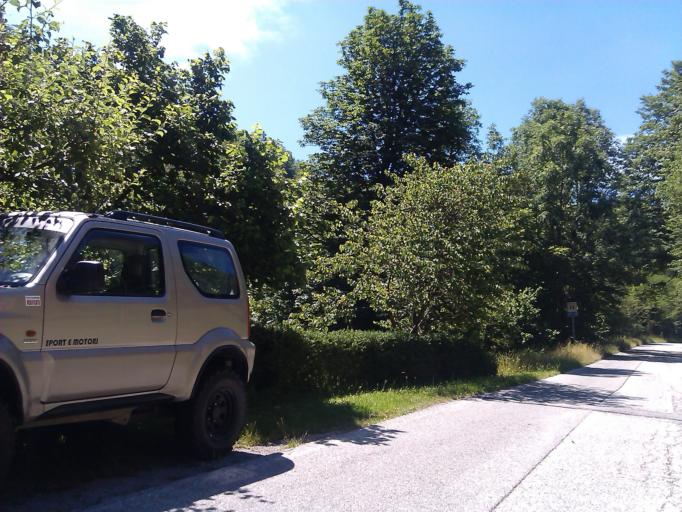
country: IT
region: Tuscany
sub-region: Provincia di Prato
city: Cantagallo
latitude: 44.0593
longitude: 11.0489
